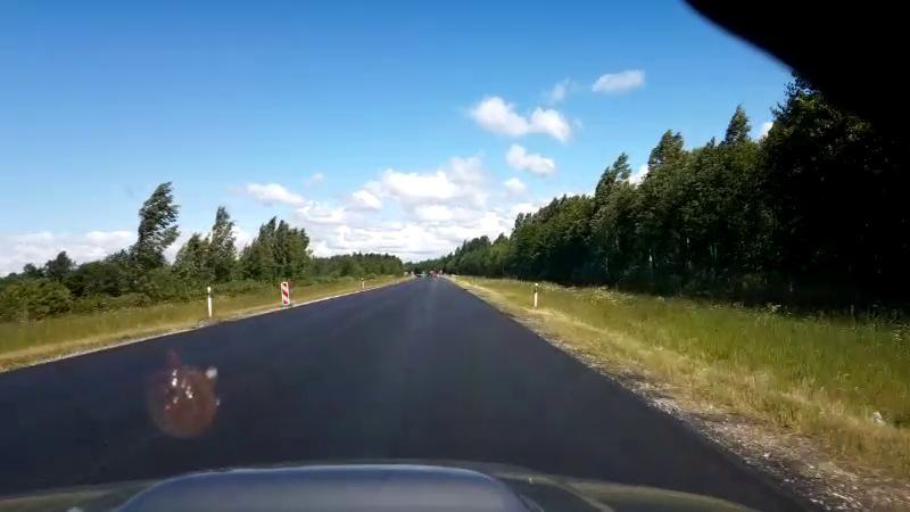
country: LV
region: Salacgrivas
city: Ainazi
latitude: 58.0080
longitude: 24.4882
